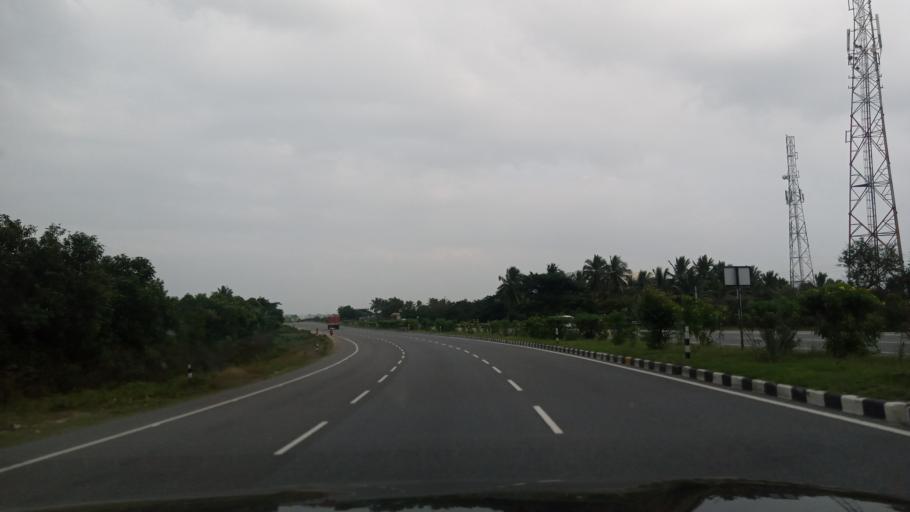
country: IN
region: Tamil Nadu
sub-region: Vellore
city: Jolarpettai
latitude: 12.5541
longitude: 78.4549
